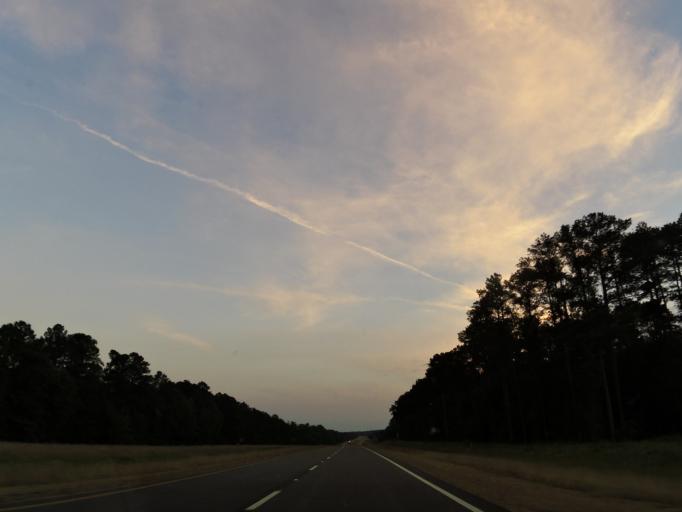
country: US
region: Mississippi
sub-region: Kemper County
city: De Kalb
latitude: 32.7125
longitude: -88.4811
